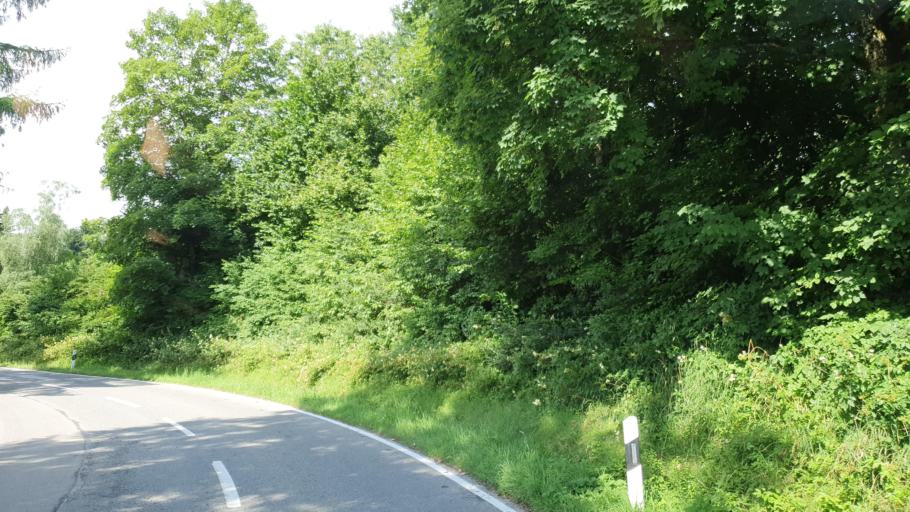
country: AT
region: Vorarlberg
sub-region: Politischer Bezirk Bregenz
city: Sulzberg
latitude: 47.5356
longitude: 9.8654
